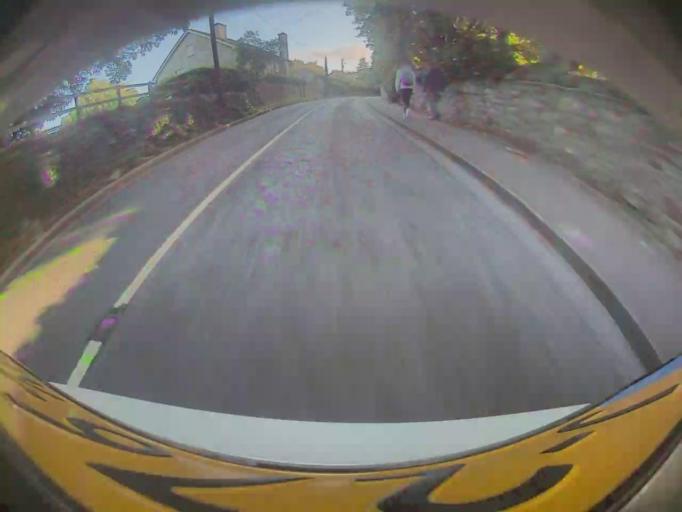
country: IE
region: Leinster
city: Sandyford
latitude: 53.2584
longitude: -6.2131
